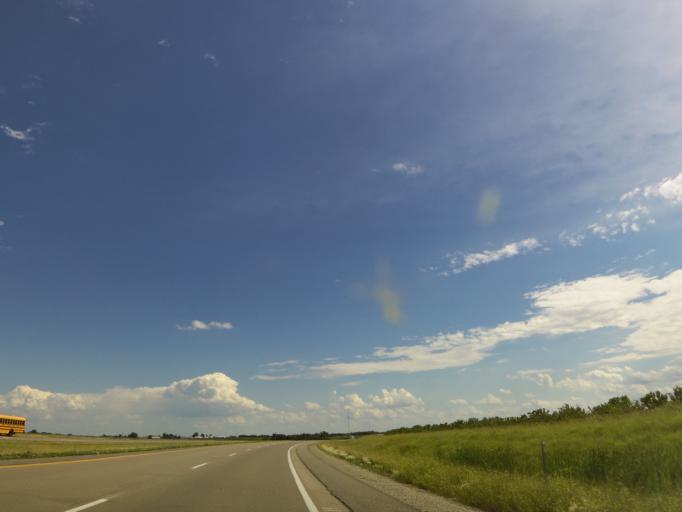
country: US
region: Iowa
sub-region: Henry County
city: Winfield
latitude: 41.2325
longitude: -91.5299
